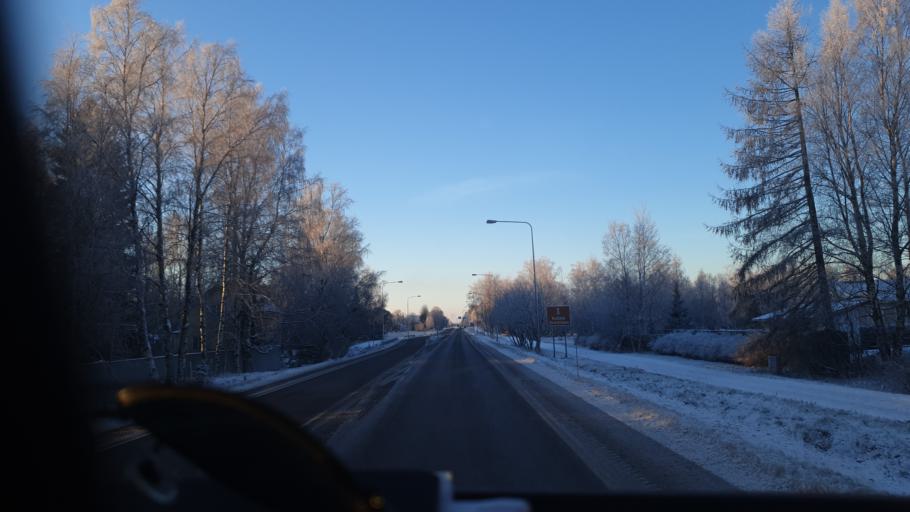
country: FI
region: Northern Ostrobothnia
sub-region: Ylivieska
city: Kalajoki
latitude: 64.2542
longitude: 23.9314
